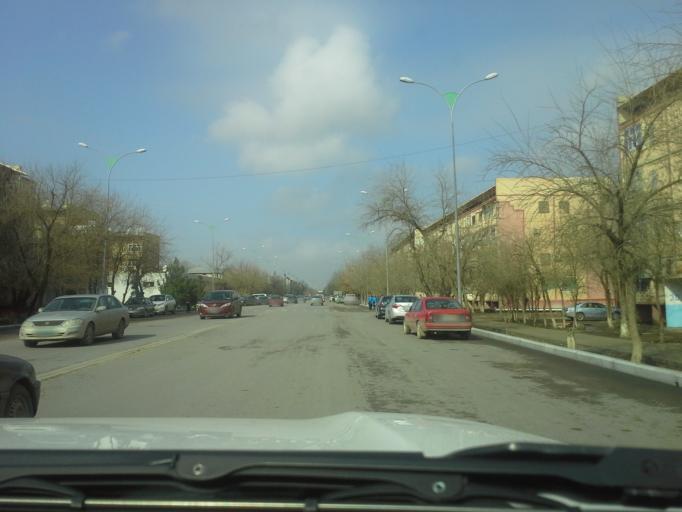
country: TM
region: Mary
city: Mary
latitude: 37.5925
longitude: 61.8330
